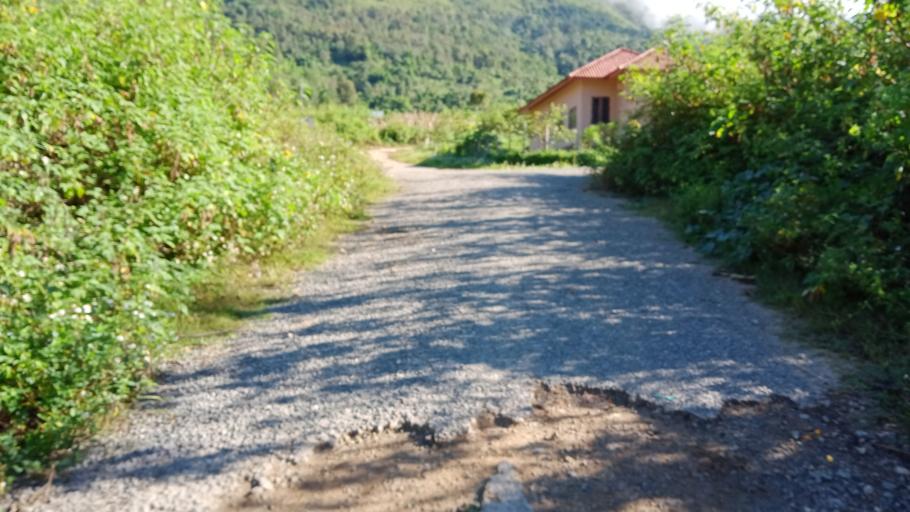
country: LA
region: Xiangkhoang
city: Phonsavan
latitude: 19.1179
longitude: 102.9104
